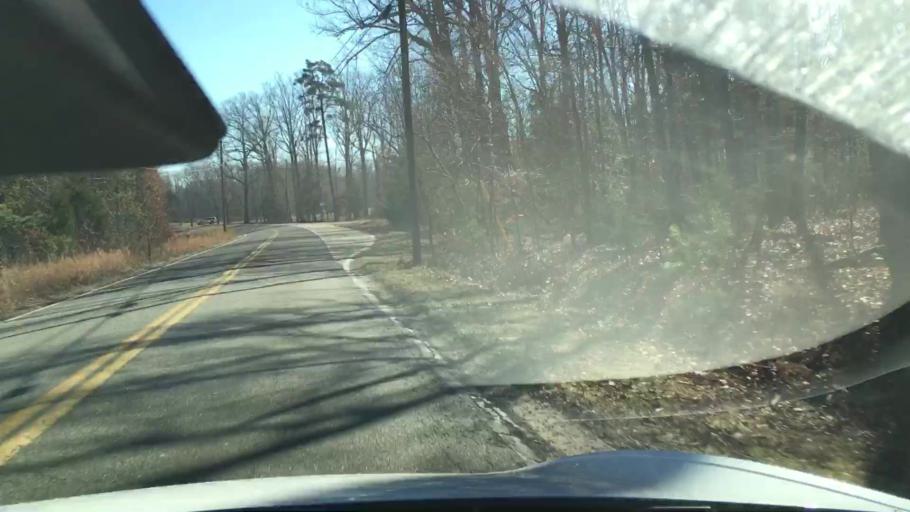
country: US
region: Virginia
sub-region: Henrico County
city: Short Pump
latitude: 37.5883
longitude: -77.7549
